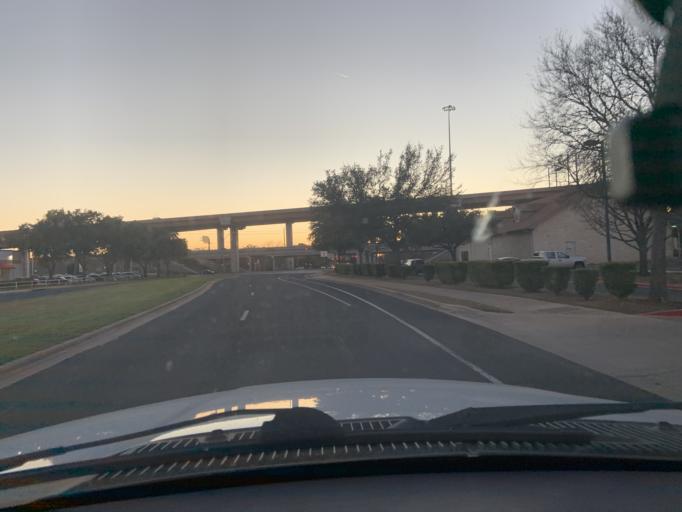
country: US
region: Texas
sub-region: Williamson County
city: Anderson Mill
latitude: 30.4663
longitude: -97.7940
